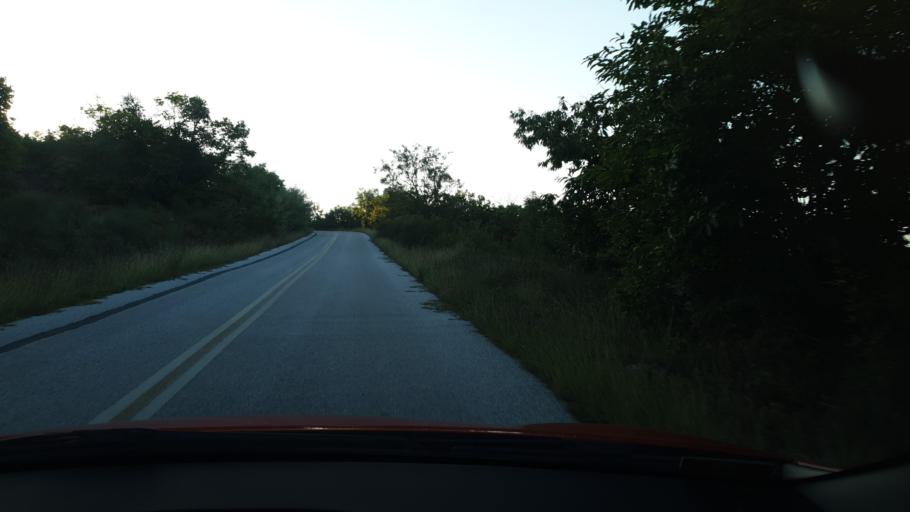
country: GR
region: Central Macedonia
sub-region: Nomos Chalkidikis
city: Galatista
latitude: 40.5186
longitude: 23.2737
